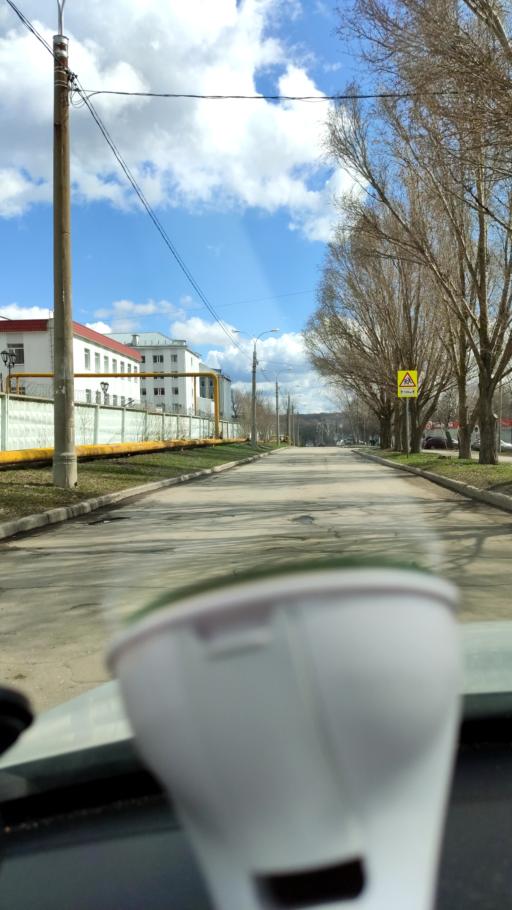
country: RU
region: Samara
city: Novosemeykino
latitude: 53.3433
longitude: 50.2253
